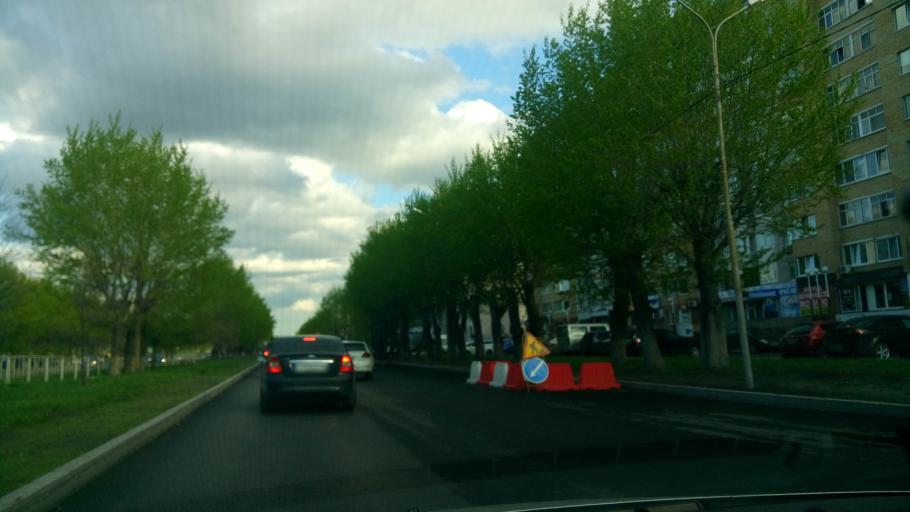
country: RU
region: Tjumen
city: Tyumen
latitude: 57.1370
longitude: 65.5978
